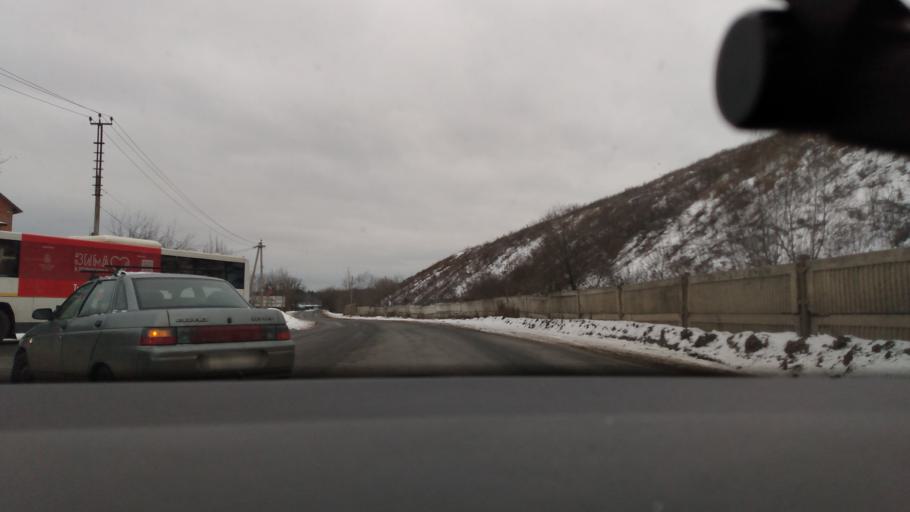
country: RU
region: Moskovskaya
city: Rodniki
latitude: 55.6960
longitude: 38.0558
